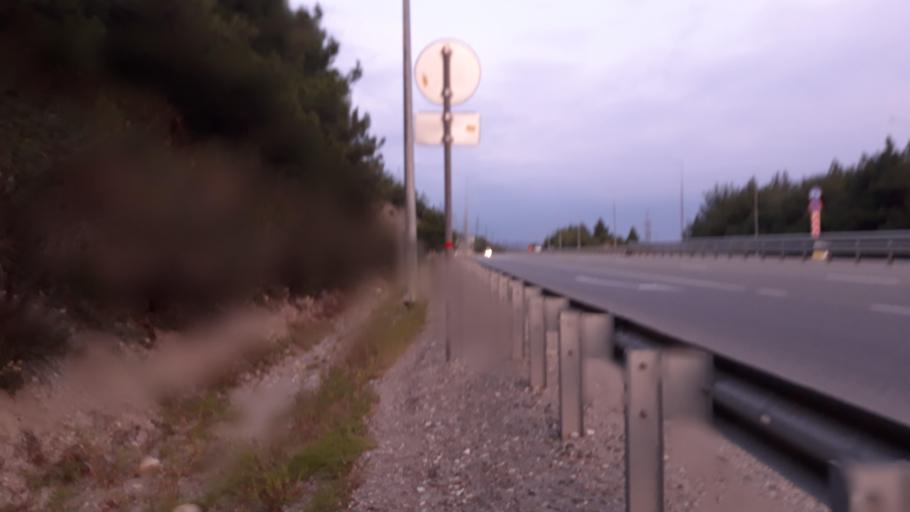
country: RU
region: Krasnodarskiy
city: Gelendzhik
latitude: 44.5779
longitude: 38.0890
